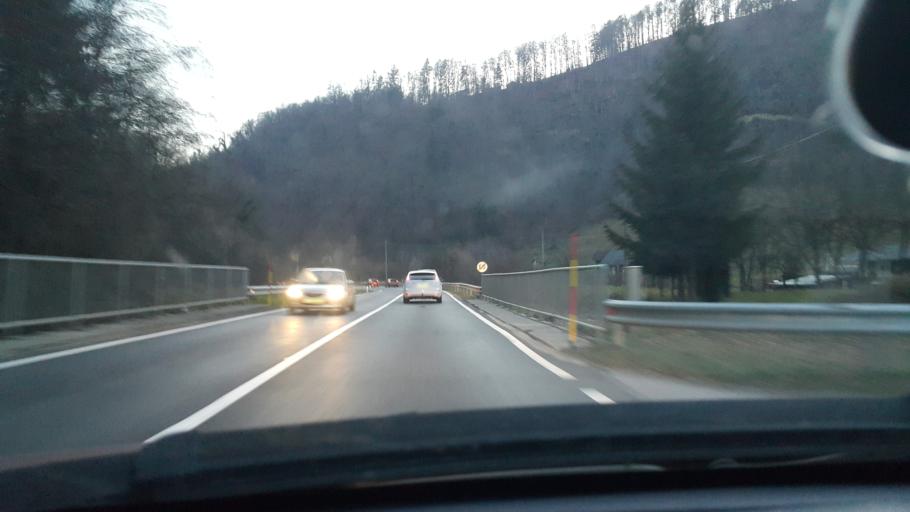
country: SI
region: Zalec
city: Gotovlje
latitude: 46.2986
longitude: 15.1711
